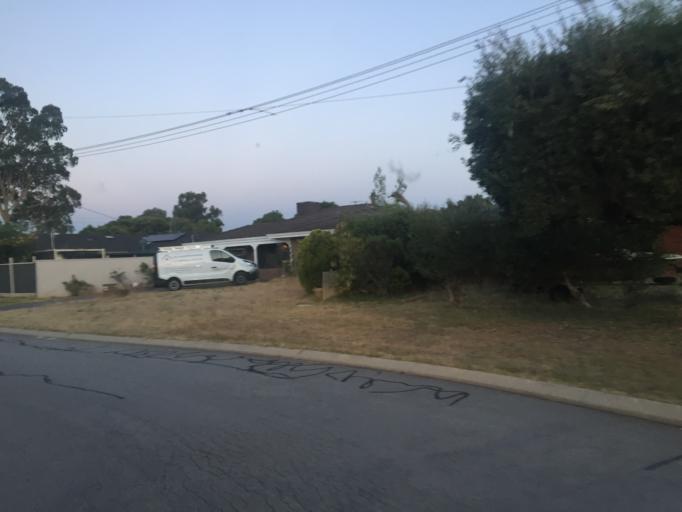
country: AU
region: Western Australia
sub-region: Gosnells
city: Maddington
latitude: -32.0314
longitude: 115.9909
